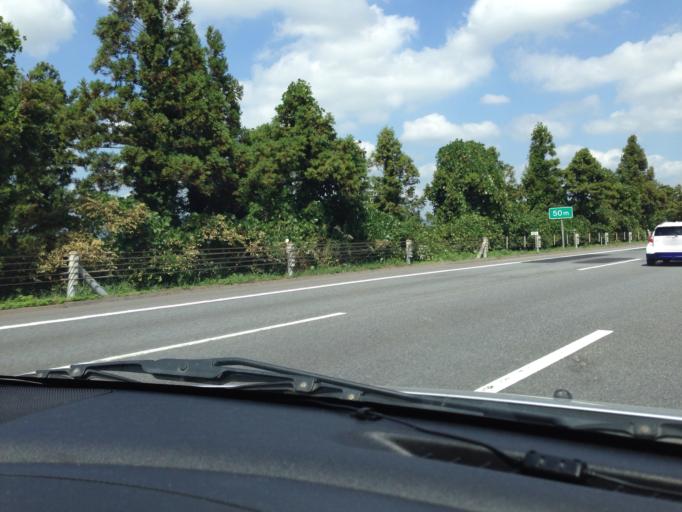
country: JP
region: Ibaraki
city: Naka
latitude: 36.0889
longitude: 140.1583
